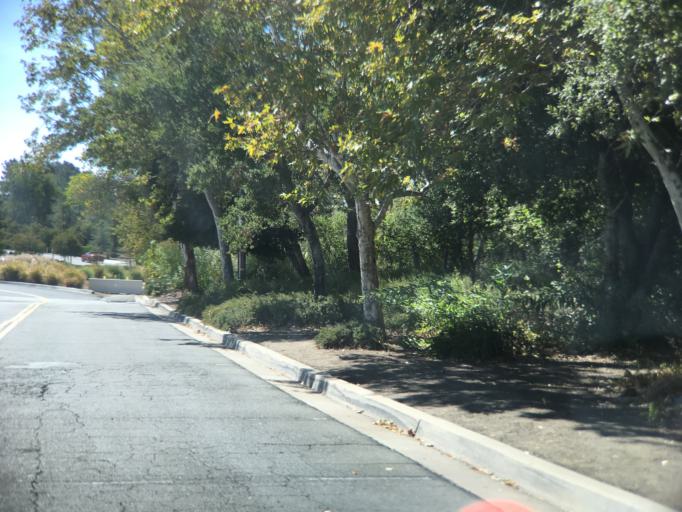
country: US
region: California
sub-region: San Diego County
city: Alpine
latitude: 32.8425
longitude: -116.7079
